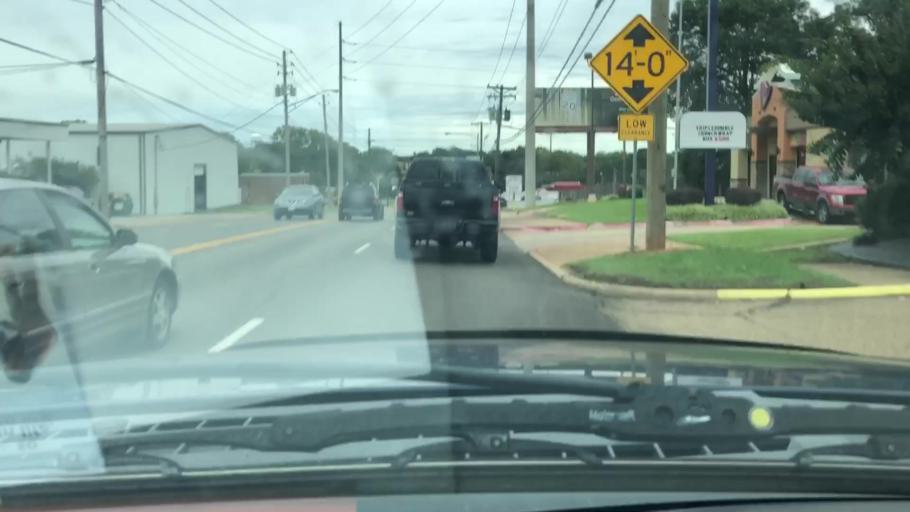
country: US
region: Texas
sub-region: Bowie County
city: Texarkana
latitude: 33.4350
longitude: -94.0606
